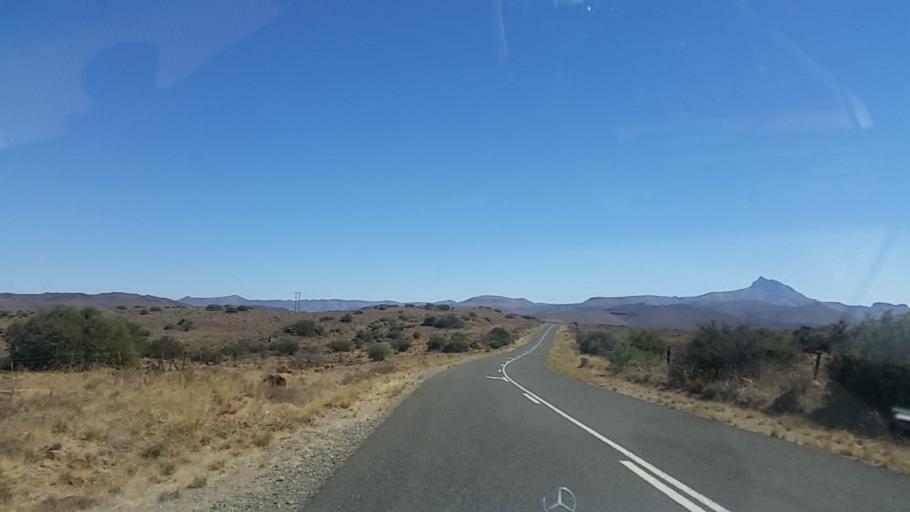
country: ZA
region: Eastern Cape
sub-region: Cacadu District Municipality
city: Graaff-Reinet
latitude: -31.9038
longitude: 24.5914
